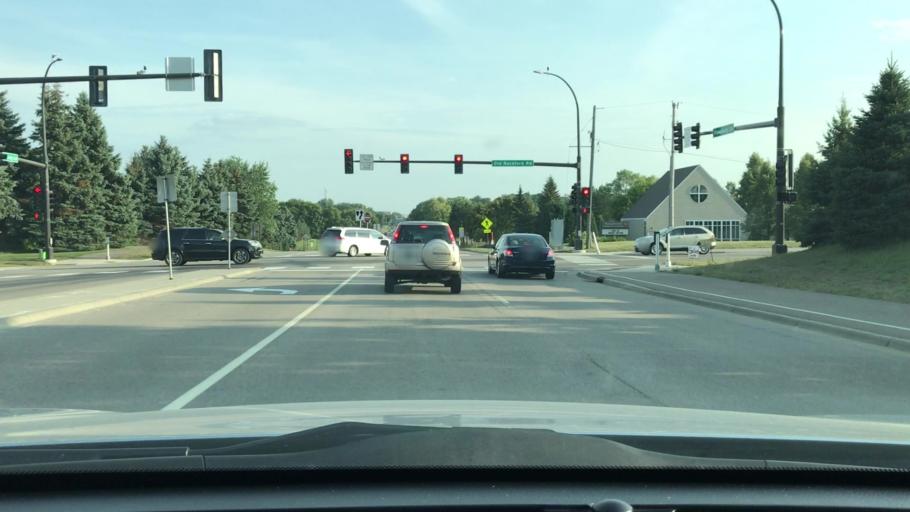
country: US
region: Minnesota
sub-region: Hennepin County
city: Plymouth
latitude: 45.0326
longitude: -93.4818
